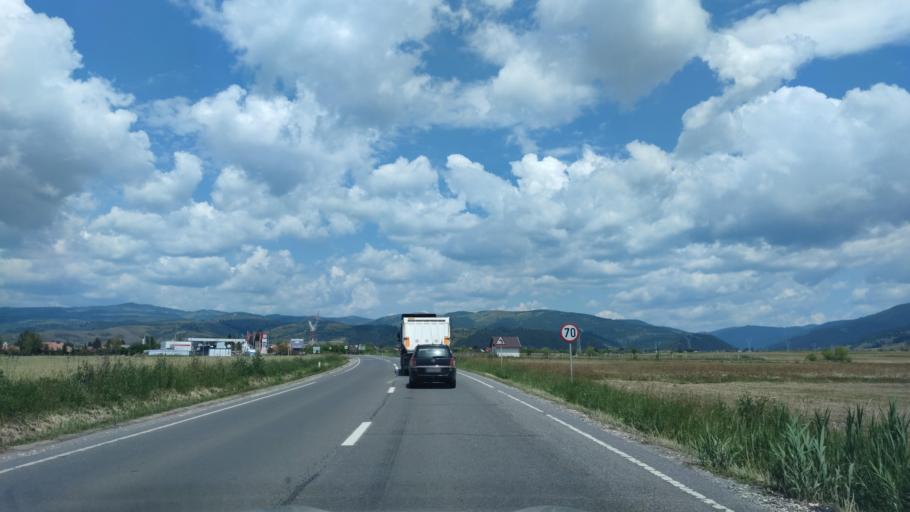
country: RO
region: Harghita
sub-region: Municipiul Gheorgheni
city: Gheorgheni
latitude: 46.7097
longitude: 25.6012
